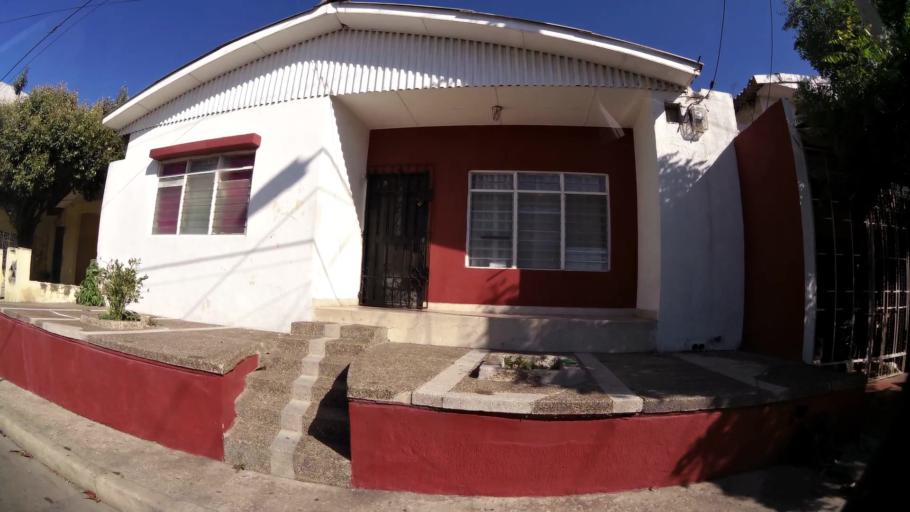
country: CO
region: Atlantico
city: Barranquilla
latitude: 10.9710
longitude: -74.7822
